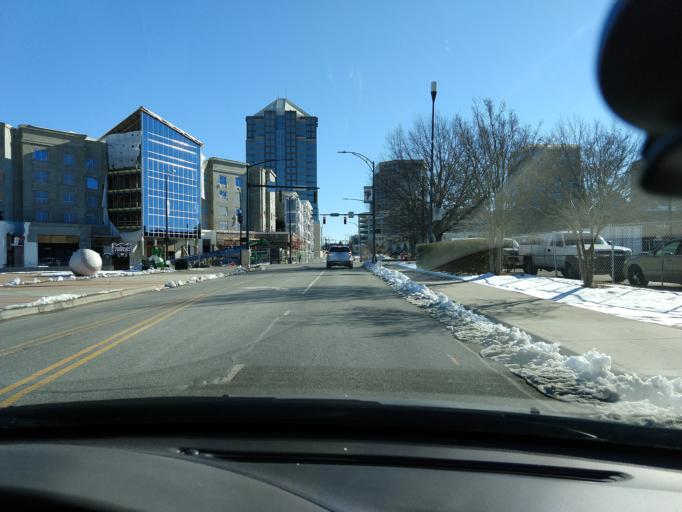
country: US
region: North Carolina
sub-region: Guilford County
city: Greensboro
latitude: 36.0756
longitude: -79.7945
